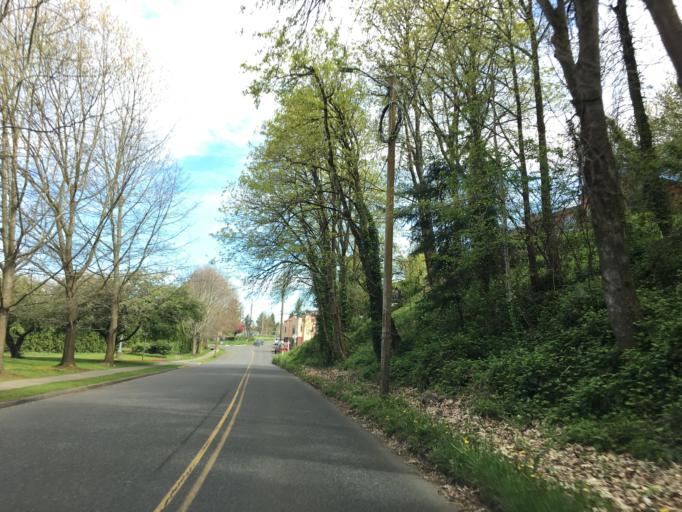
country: US
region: Oregon
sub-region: Multnomah County
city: Lents
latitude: 45.5315
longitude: -122.5934
